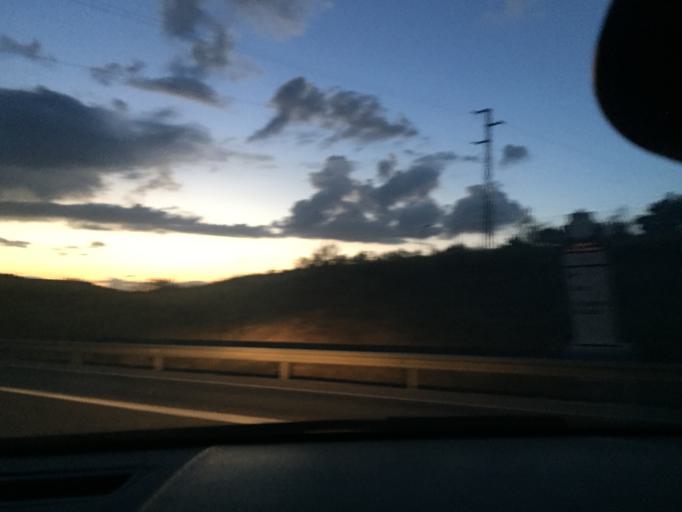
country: ES
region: Andalusia
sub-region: Provincia de Jaen
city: Mancha Real
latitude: 37.8012
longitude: -3.6610
